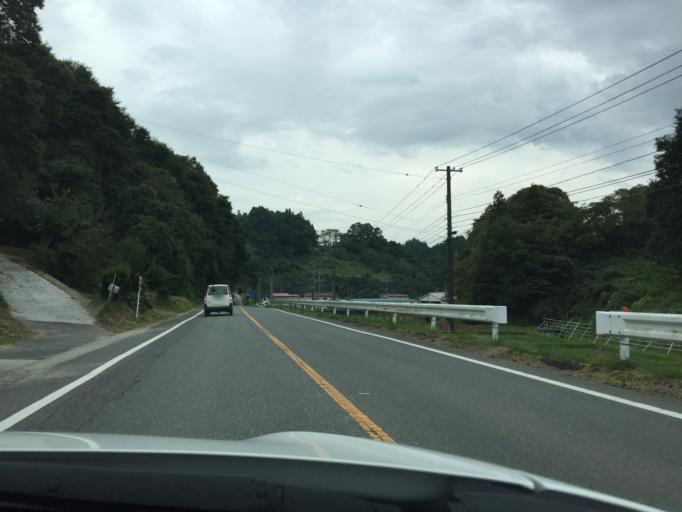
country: JP
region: Fukushima
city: Nihommatsu
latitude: 37.5951
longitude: 140.5375
